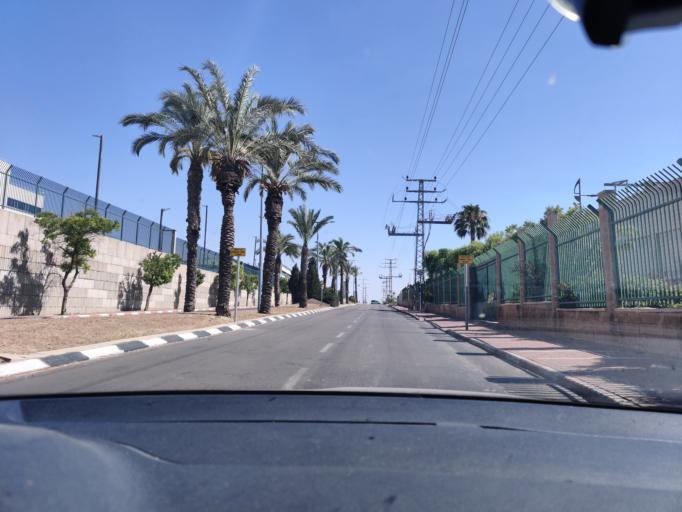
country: IL
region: Southern District
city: Qiryat Gat
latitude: 31.5967
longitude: 34.7863
